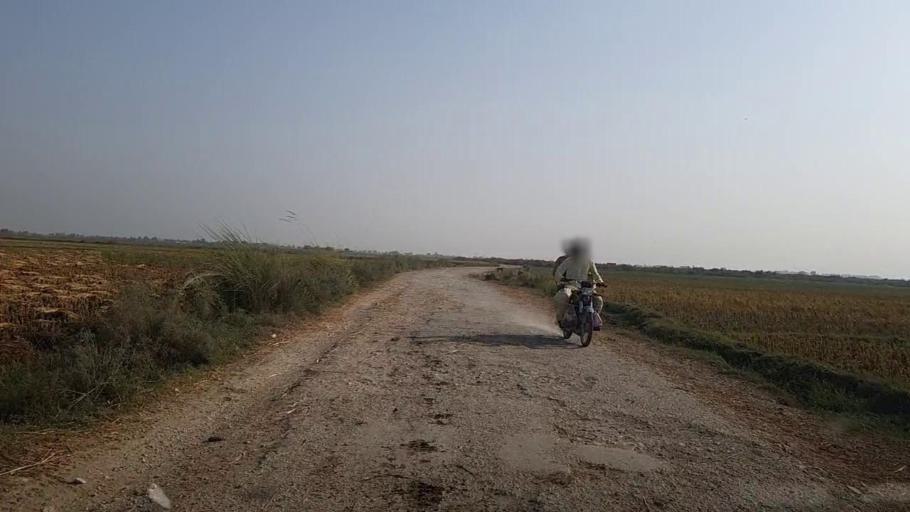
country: PK
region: Sindh
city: Kandhkot
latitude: 28.2978
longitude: 69.2523
